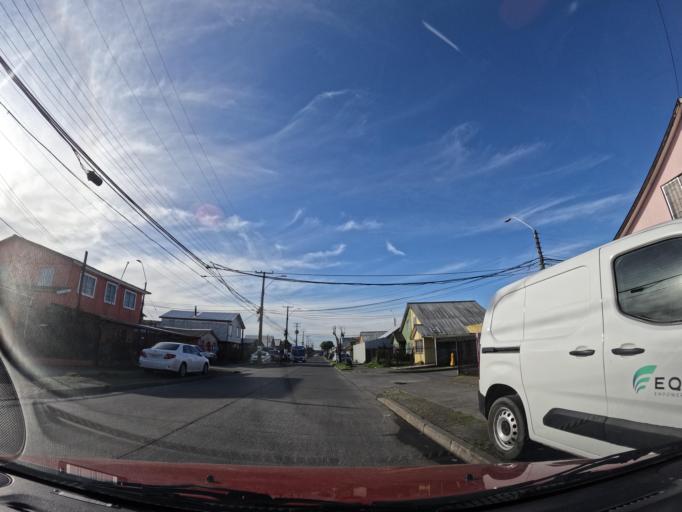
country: CL
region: Biobio
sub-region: Provincia de Concepcion
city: Talcahuano
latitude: -36.7470
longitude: -73.0858
